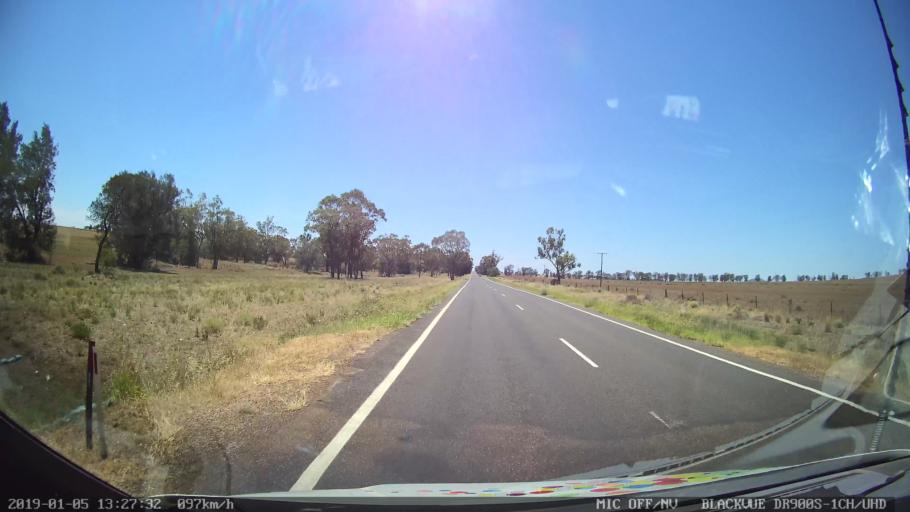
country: AU
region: New South Wales
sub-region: Gunnedah
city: Gunnedah
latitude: -31.0437
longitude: 150.0307
